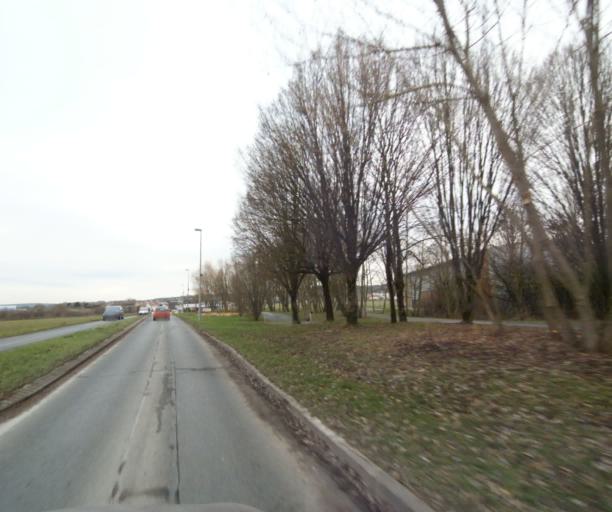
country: FR
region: Ile-de-France
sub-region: Departement de Seine-et-Marne
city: Othis
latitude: 49.0709
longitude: 2.6777
